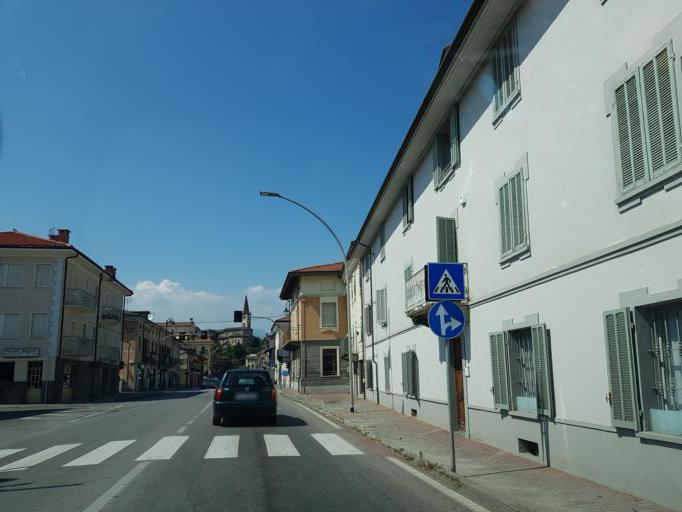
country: IT
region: Piedmont
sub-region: Provincia di Cuneo
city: Caraglio
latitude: 44.4174
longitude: 7.4342
